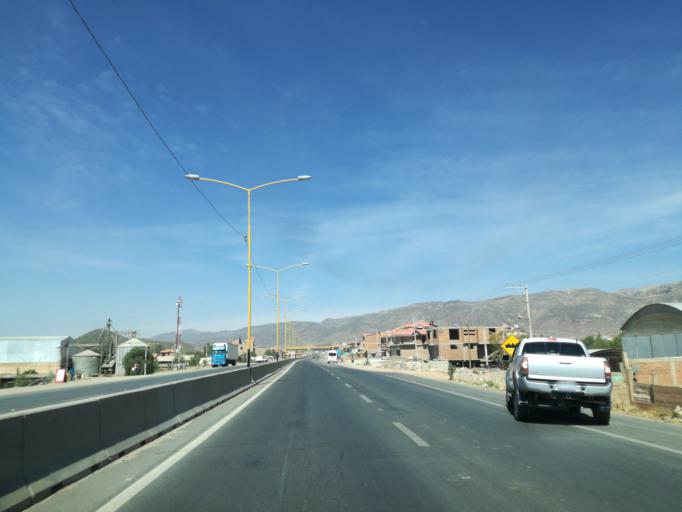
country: BO
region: Cochabamba
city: Sipe Sipe
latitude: -17.4353
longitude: -66.3345
